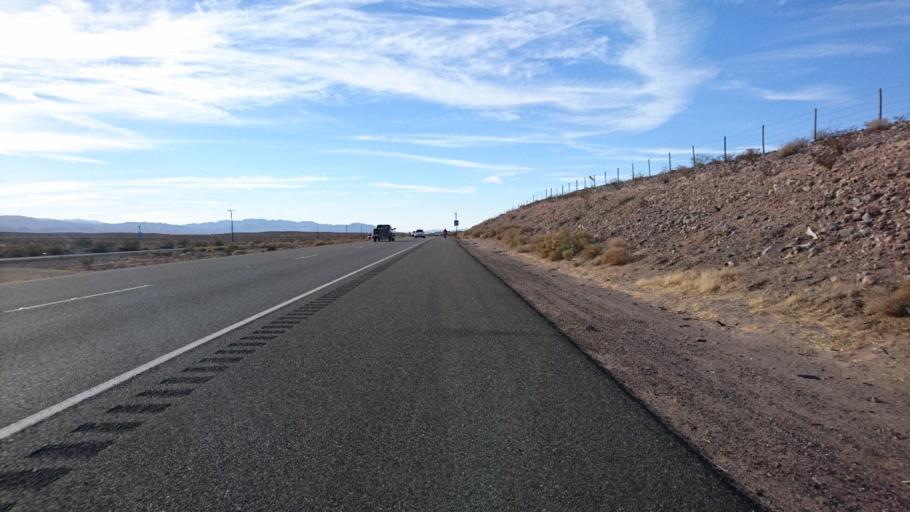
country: US
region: California
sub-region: San Bernardino County
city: Fort Irwin
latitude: 34.7819
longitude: -116.4075
